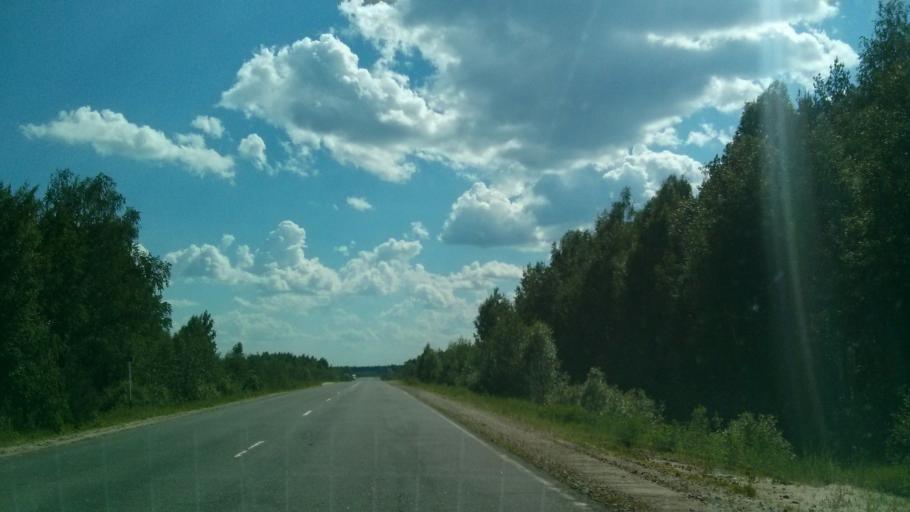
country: RU
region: Vladimir
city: Melenki
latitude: 55.3440
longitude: 41.6704
